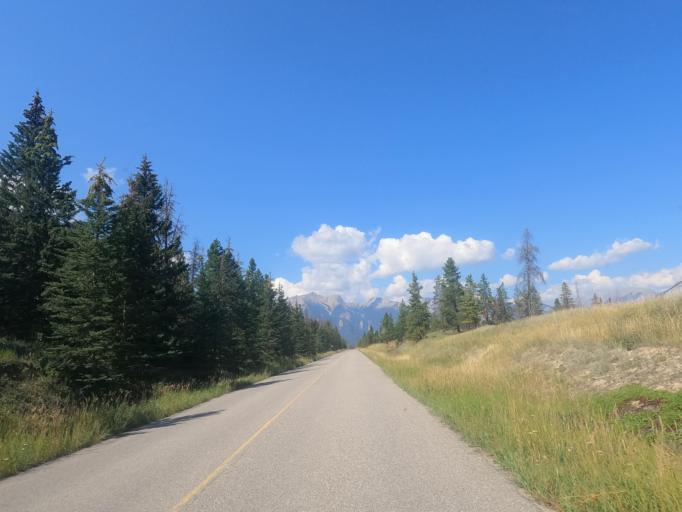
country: CA
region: Alberta
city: Jasper Park Lodge
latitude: 52.9745
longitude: -118.0631
